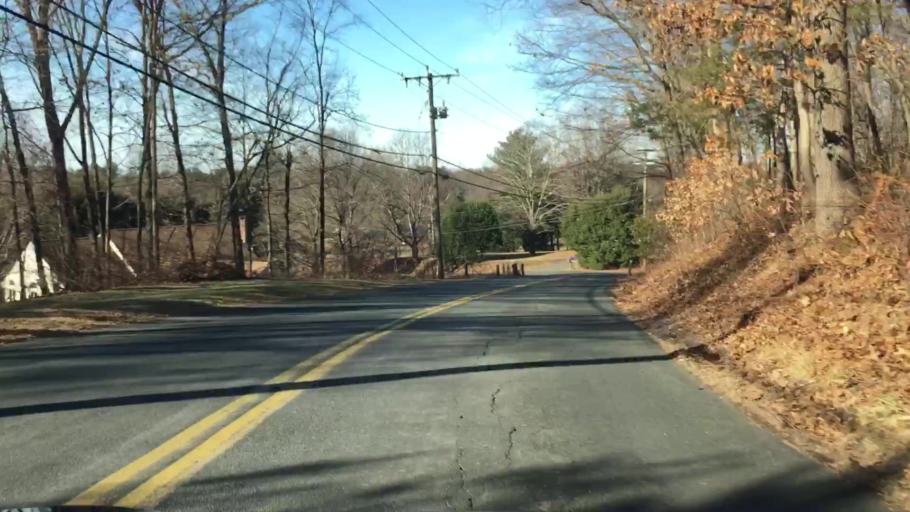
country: US
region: Connecticut
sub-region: Tolland County
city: Somers
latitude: 41.9718
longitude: -72.4420
